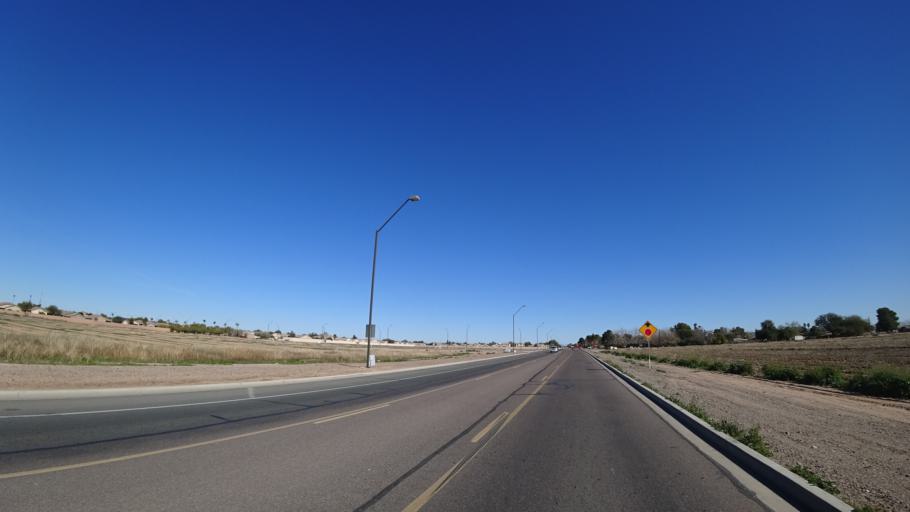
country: US
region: Arizona
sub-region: Maricopa County
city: Avondale
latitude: 33.4207
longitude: -112.3084
